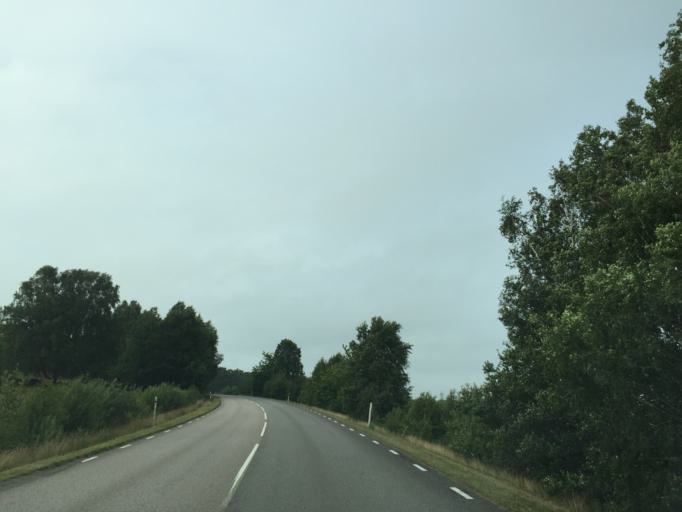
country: SE
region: Halland
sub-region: Falkenbergs Kommun
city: Falkenberg
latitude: 56.8781
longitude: 12.5601
